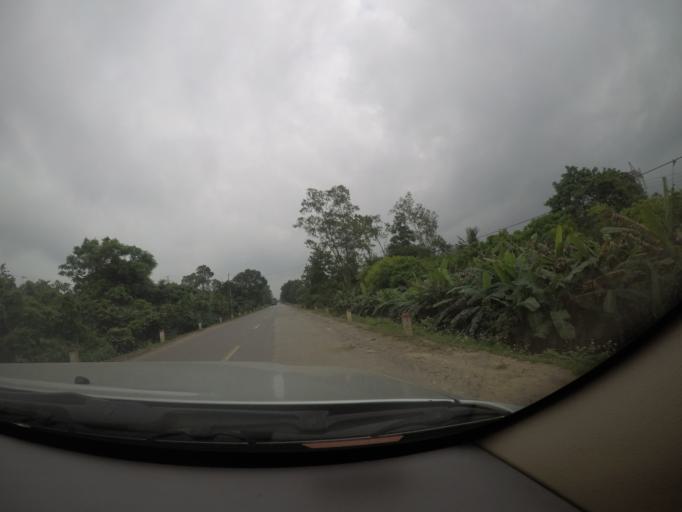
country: VN
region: Quang Binh
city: Kien Giang
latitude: 17.1869
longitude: 106.7302
